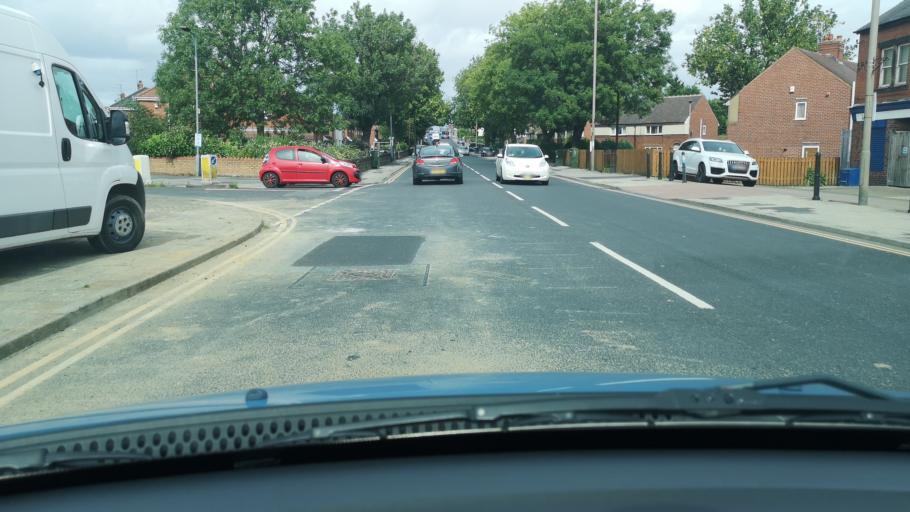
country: GB
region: England
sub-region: Barnsley
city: Cudworth
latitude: 53.5598
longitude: -1.4369
